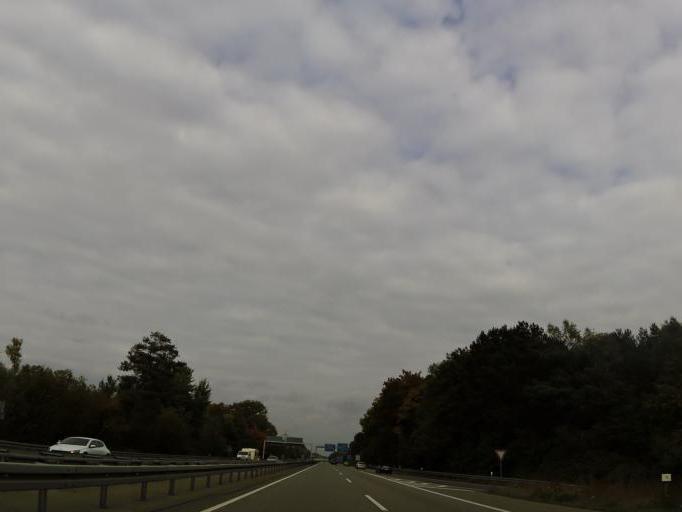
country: DE
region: Saarland
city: Kirkel
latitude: 49.3079
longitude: 7.2523
